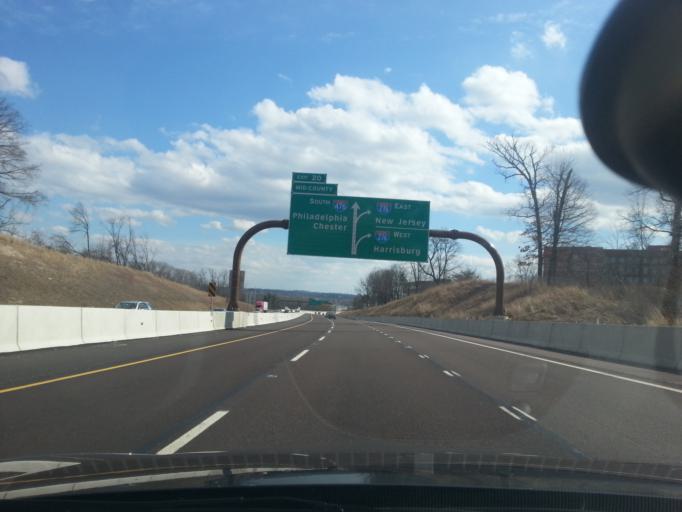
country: US
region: Pennsylvania
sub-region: Montgomery County
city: Plymouth Meeting
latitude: 40.1223
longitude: -75.2825
